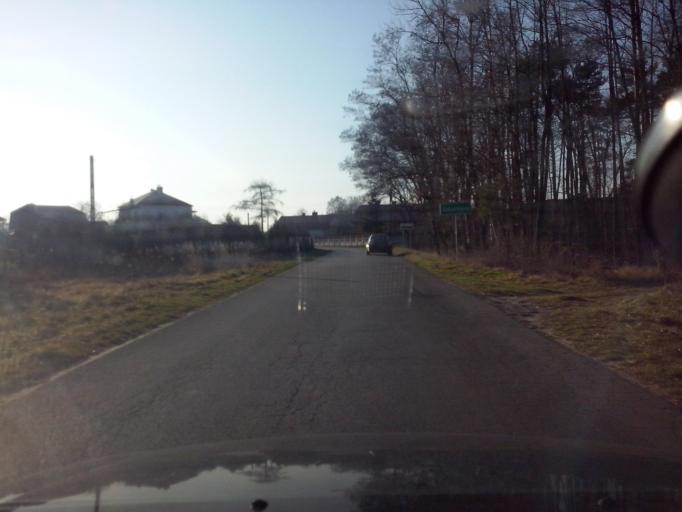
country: PL
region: Subcarpathian Voivodeship
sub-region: Powiat lezajski
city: Letownia
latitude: 50.3435
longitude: 22.2001
